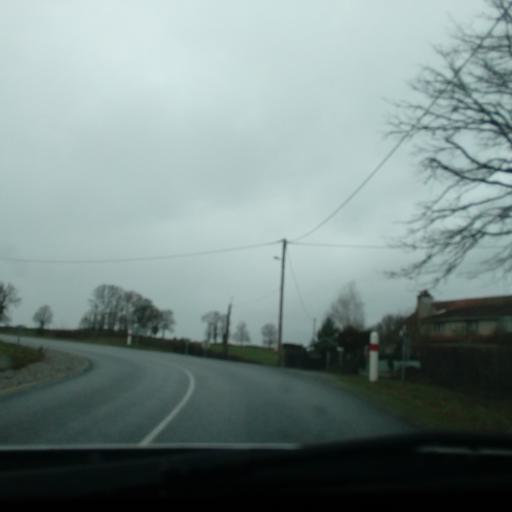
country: FR
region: Limousin
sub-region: Departement de la Creuse
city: Sainte-Feyre
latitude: 46.1714
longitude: 1.9547
